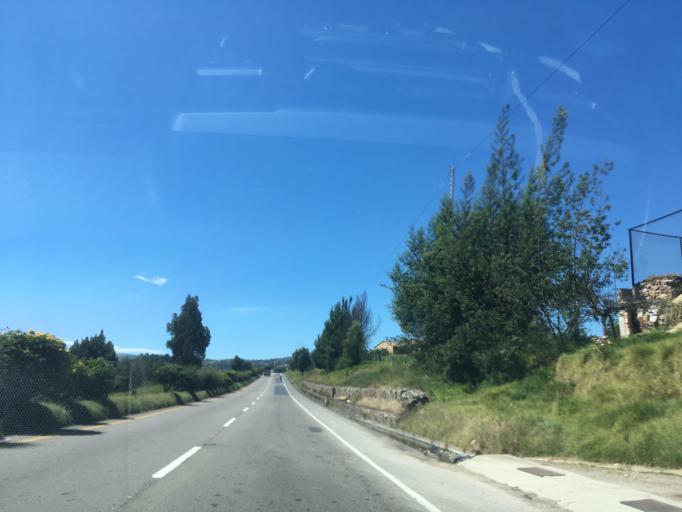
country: CO
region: Boyaca
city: Tuta
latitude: 5.6896
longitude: -73.2565
